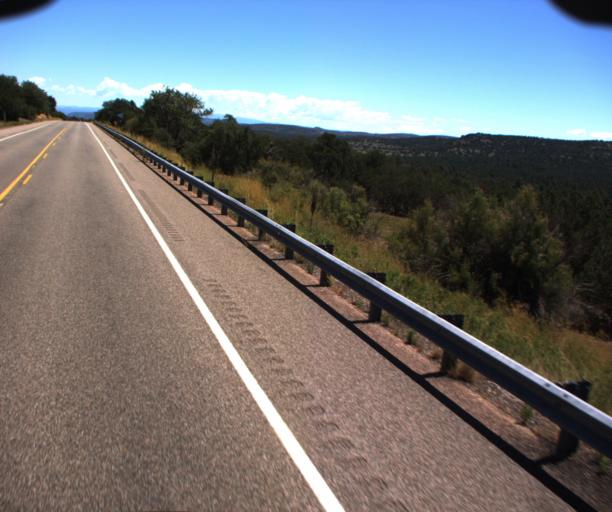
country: US
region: Arizona
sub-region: Navajo County
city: Cibecue
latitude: 33.6959
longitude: -110.5553
